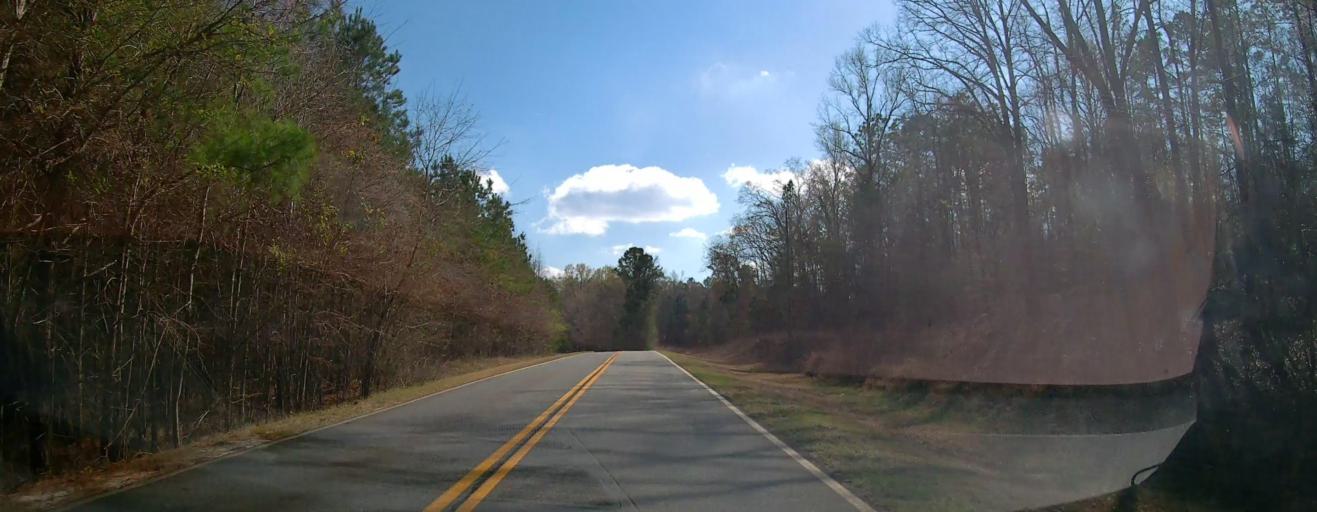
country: US
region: Georgia
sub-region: Twiggs County
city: Jeffersonville
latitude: 32.7298
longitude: -83.3495
